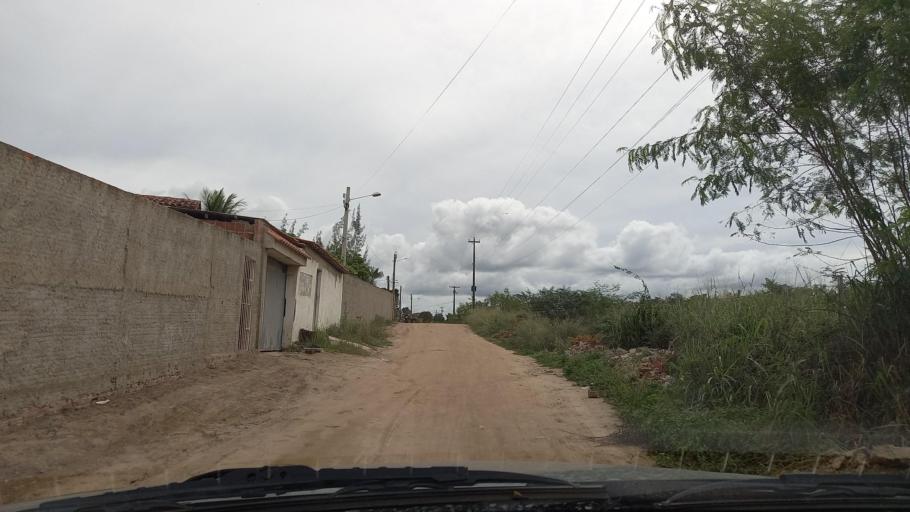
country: BR
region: Pernambuco
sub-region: Gravata
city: Gravata
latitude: -8.1915
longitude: -35.5961
